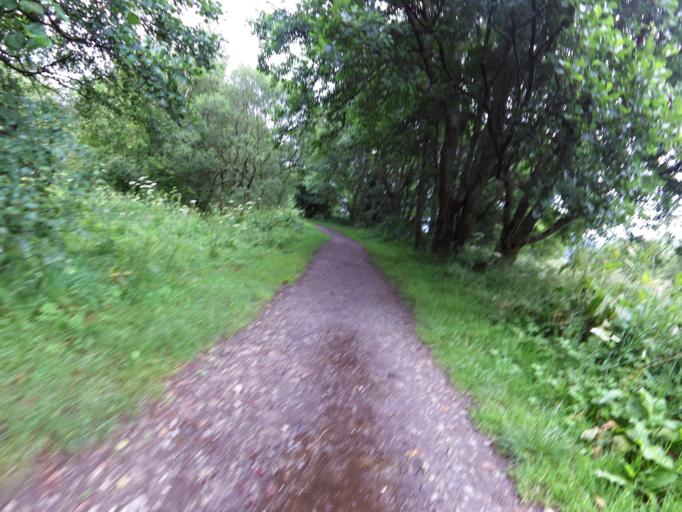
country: GB
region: Scotland
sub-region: Highland
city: Fort William
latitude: 56.8291
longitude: -5.0930
